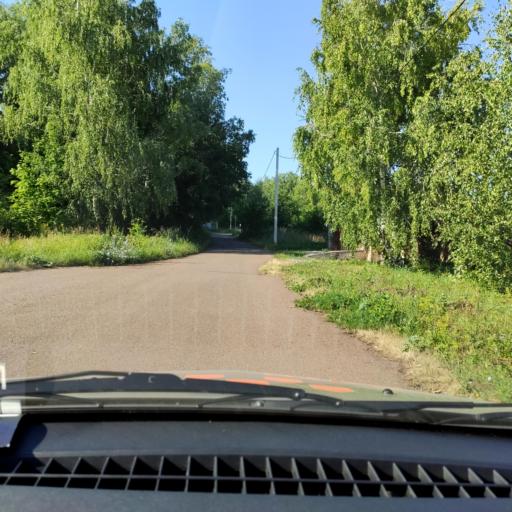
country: RU
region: Bashkortostan
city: Avdon
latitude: 54.5926
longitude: 55.6957
